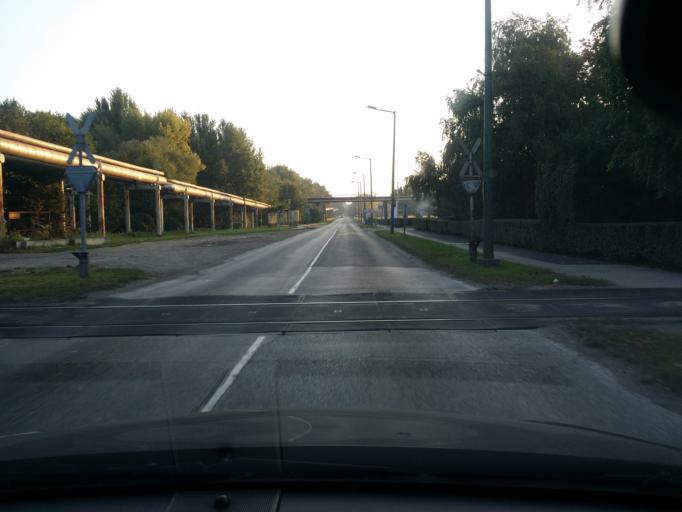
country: HU
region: Fejer
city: Dunaujvaros
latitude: 46.9288
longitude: 18.9391
